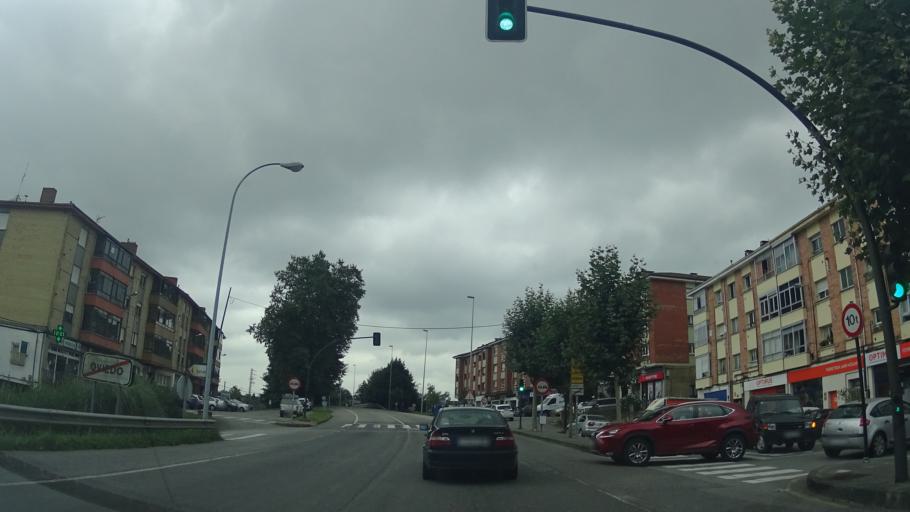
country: ES
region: Asturias
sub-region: Province of Asturias
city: Lugones
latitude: 43.3789
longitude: -5.7930
